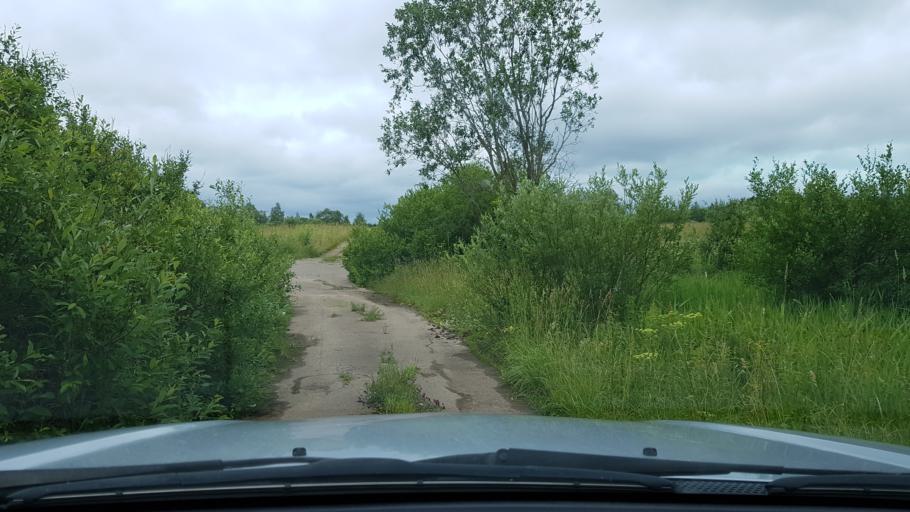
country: EE
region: Ida-Virumaa
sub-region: Narva-Joesuu linn
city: Narva-Joesuu
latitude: 59.3465
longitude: 28.0298
